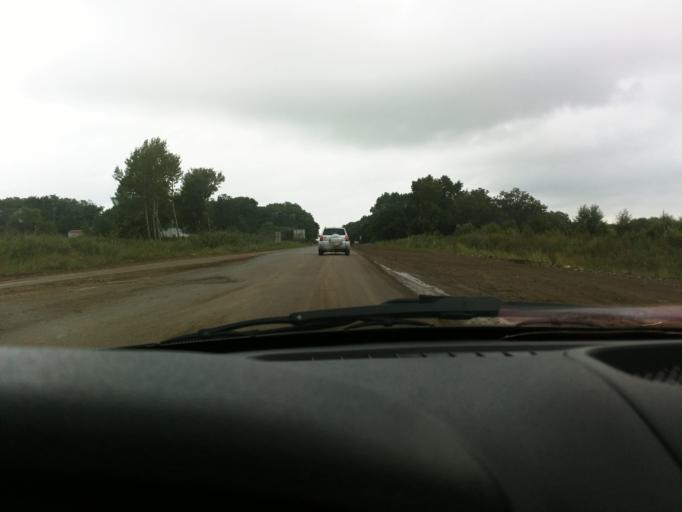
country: RU
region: Primorskiy
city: Dal'nerechensk
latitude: 45.8875
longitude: 133.7321
